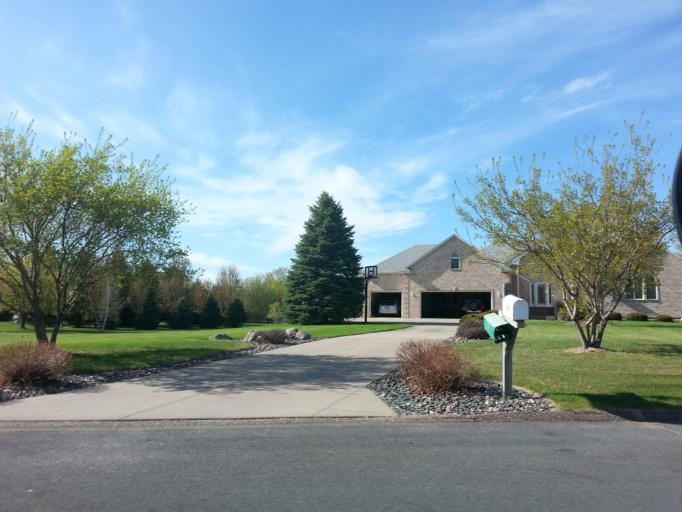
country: US
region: Minnesota
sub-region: Washington County
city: Lake Elmo
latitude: 44.9841
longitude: -92.8536
